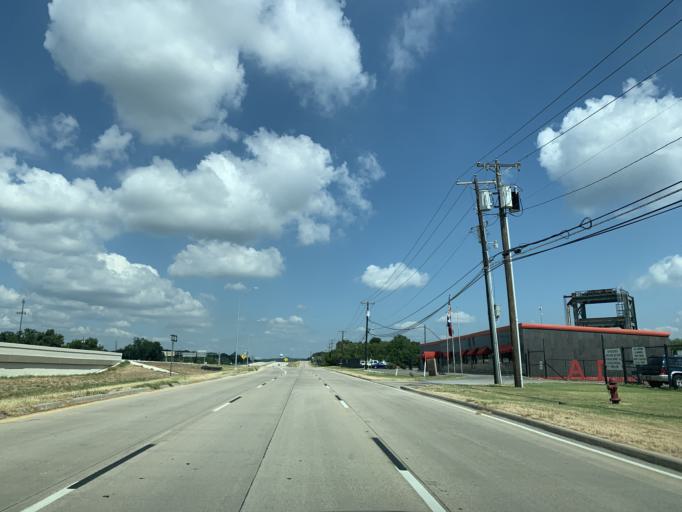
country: US
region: Texas
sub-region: Tarrant County
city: Lakeside
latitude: 32.8402
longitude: -97.4935
